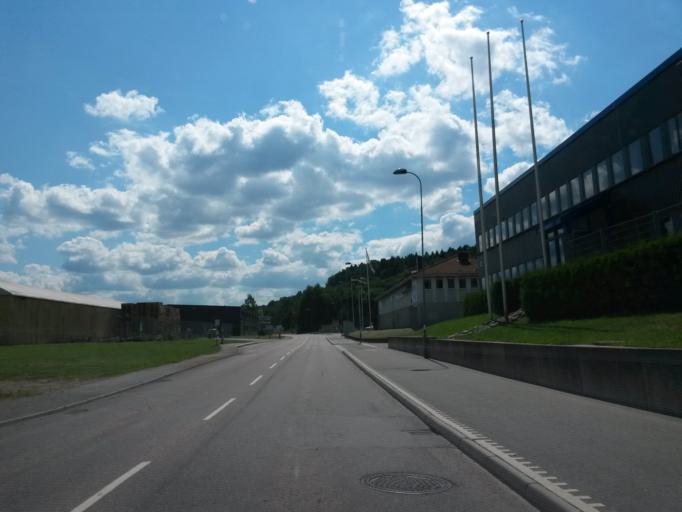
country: SE
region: Vaestra Goetaland
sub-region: Goteborg
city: Hammarkullen
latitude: 57.7704
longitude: 11.9925
